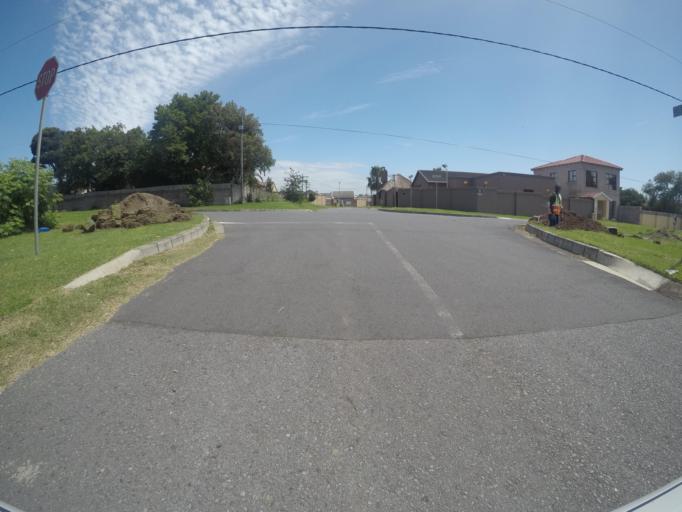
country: ZA
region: Eastern Cape
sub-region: Buffalo City Metropolitan Municipality
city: East London
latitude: -32.9500
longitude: 27.9997
